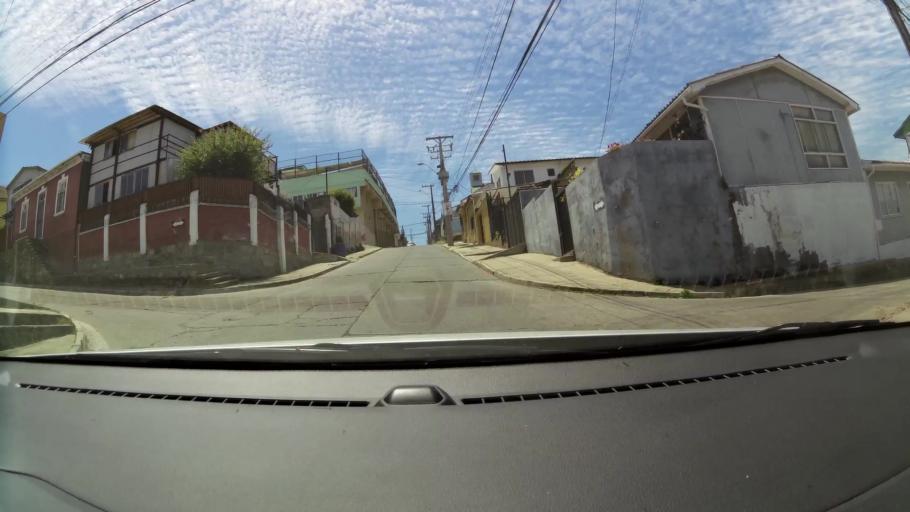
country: CL
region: Valparaiso
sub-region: Provincia de Valparaiso
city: Valparaiso
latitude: -33.0475
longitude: -71.5971
